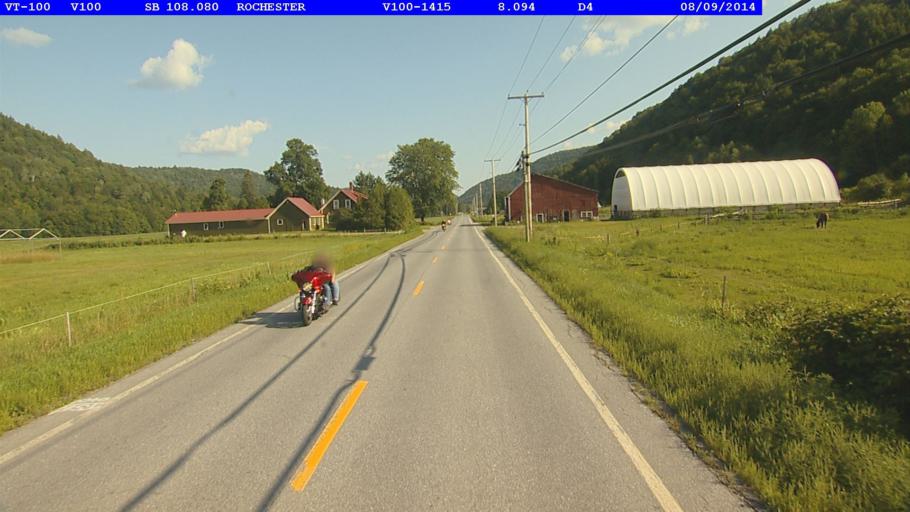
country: US
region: Vermont
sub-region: Orange County
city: Randolph
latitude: 43.9092
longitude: -72.8305
